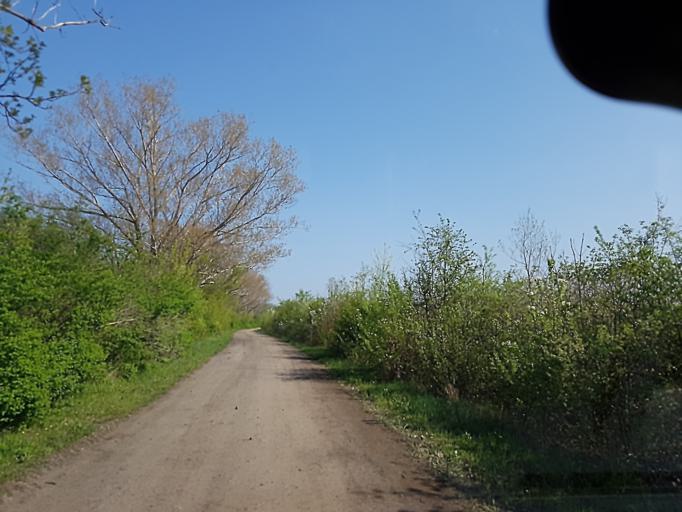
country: DE
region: Brandenburg
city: Muhlberg
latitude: 51.4456
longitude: 13.2367
